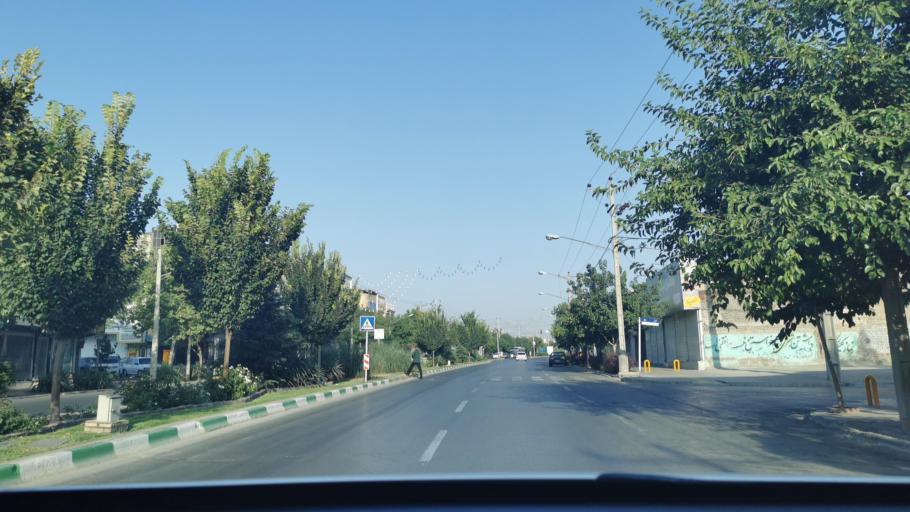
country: IR
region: Razavi Khorasan
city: Mashhad
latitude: 36.3519
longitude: 59.5154
